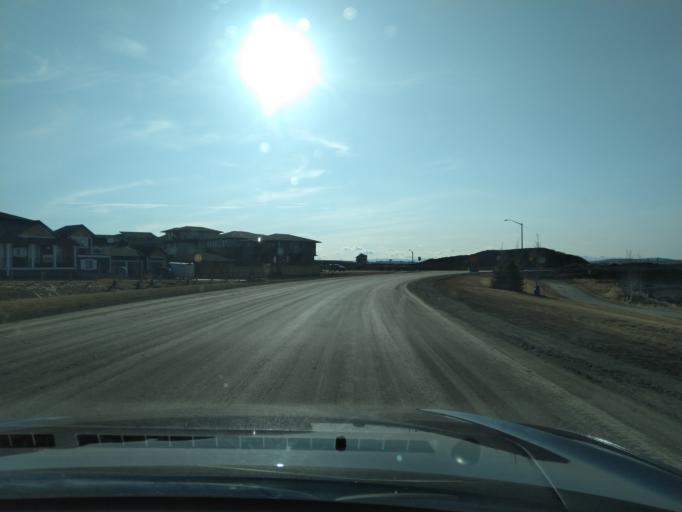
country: CA
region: Alberta
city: Cochrane
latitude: 51.1135
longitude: -114.3973
